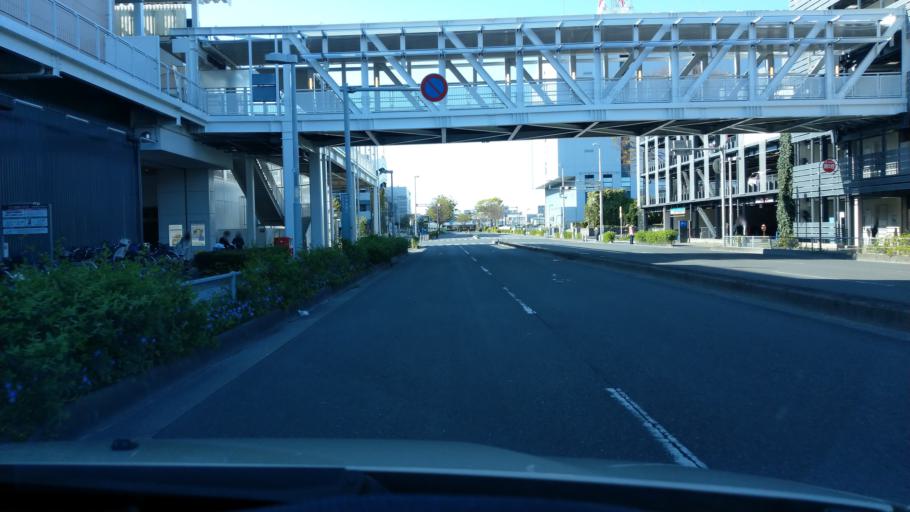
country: JP
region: Saitama
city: Yono
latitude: 35.8950
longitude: 139.6372
